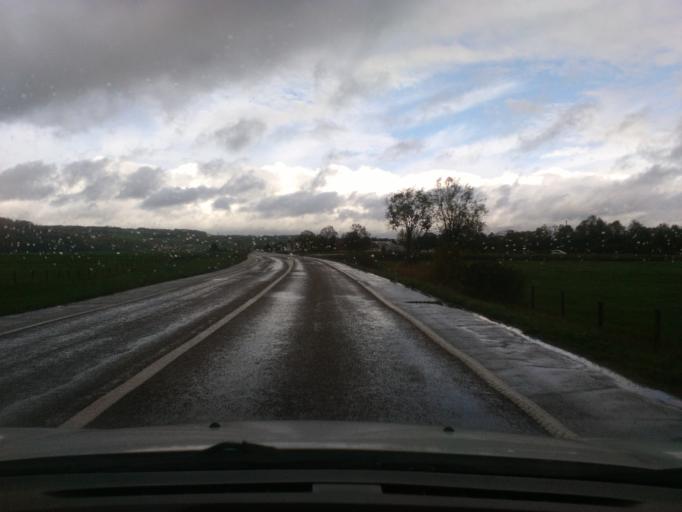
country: FR
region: Lorraine
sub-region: Departement des Vosges
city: Charmes
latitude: 48.3750
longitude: 6.2726
